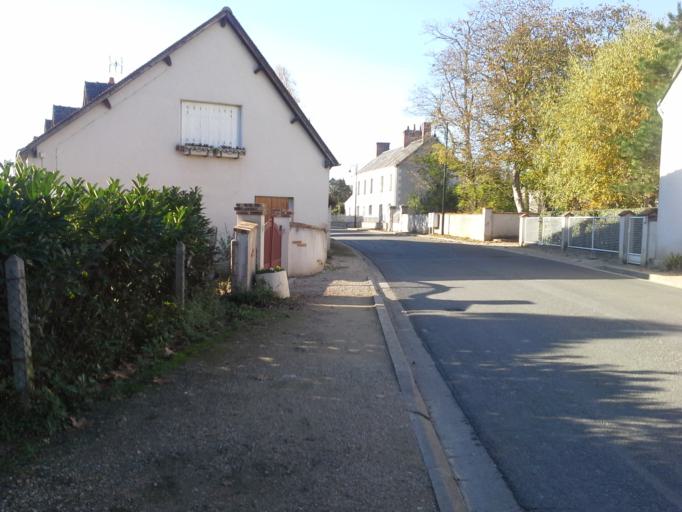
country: FR
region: Centre
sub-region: Departement du Loir-et-Cher
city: Saint-Romain-sur-Cher
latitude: 47.3632
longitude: 1.4018
